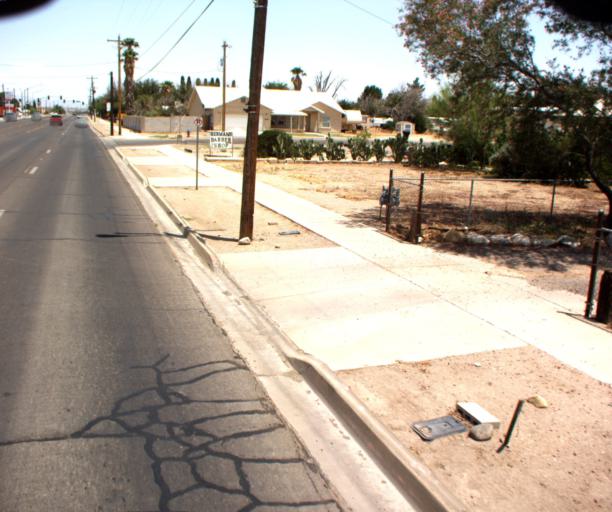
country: US
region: Arizona
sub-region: Graham County
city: Thatcher
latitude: 32.8491
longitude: -109.7576
